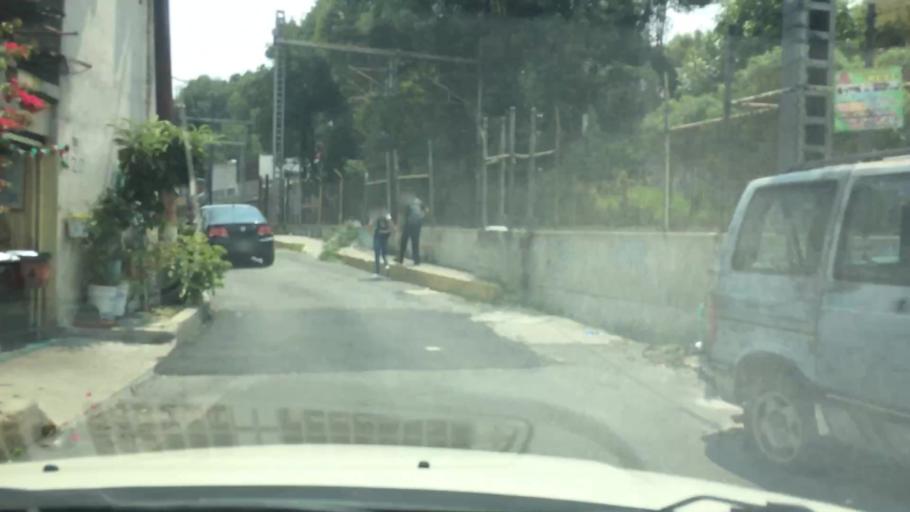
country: MX
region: Mexico City
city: Xochimilco
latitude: 19.2706
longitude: -99.1290
